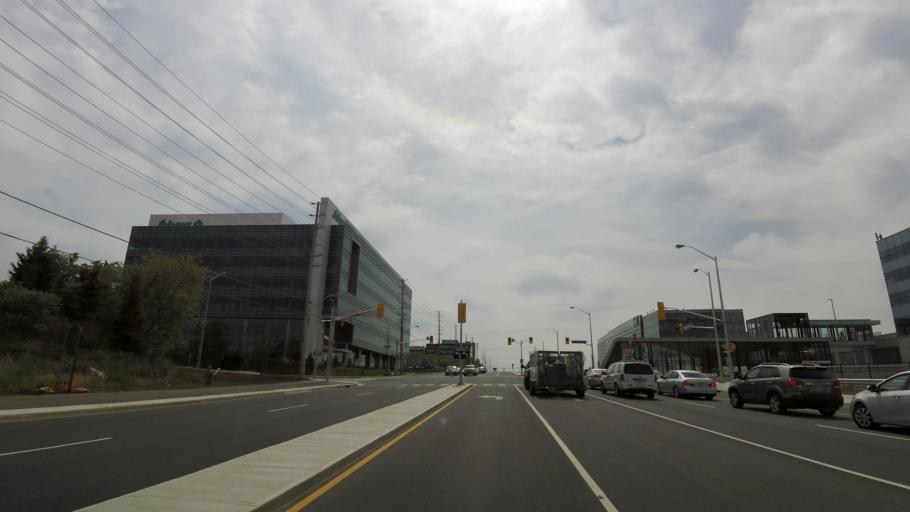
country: CA
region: Ontario
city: Etobicoke
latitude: 43.6451
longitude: -79.6101
